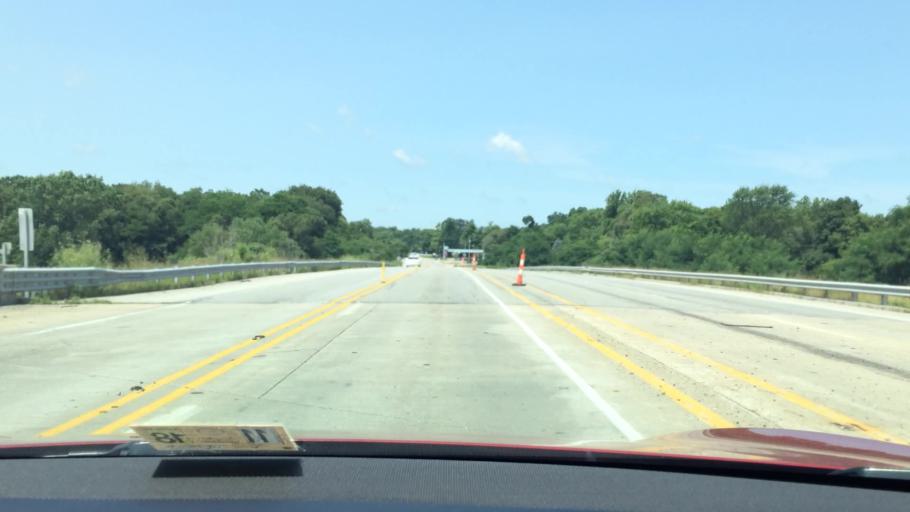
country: US
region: Indiana
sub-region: LaPorte County
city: Hudson Lake
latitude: 41.6707
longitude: -86.6163
